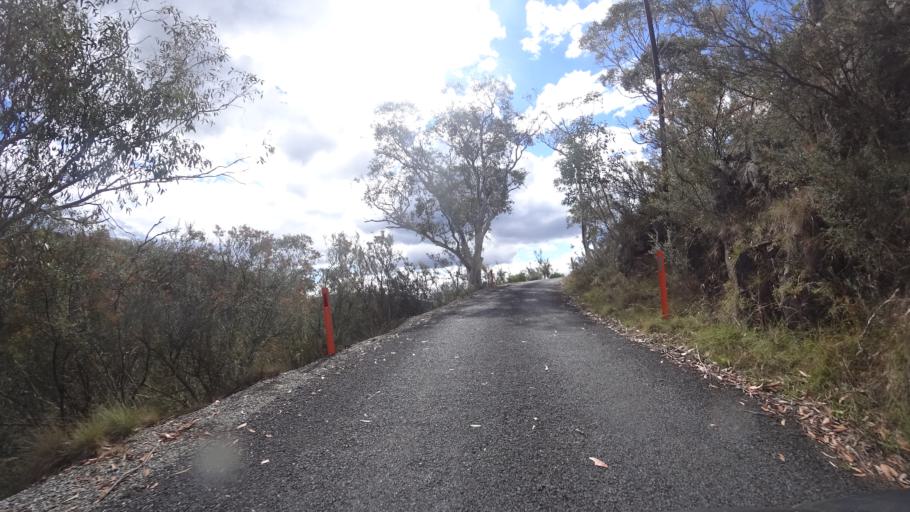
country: AU
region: New South Wales
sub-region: Tumut Shire
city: Tumut
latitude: -35.7233
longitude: 148.4872
